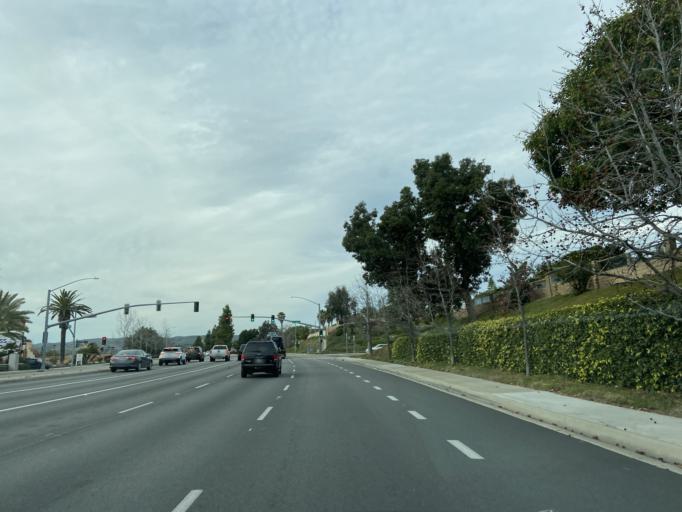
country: US
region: California
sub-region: San Diego County
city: Vista
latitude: 33.2464
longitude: -117.2905
